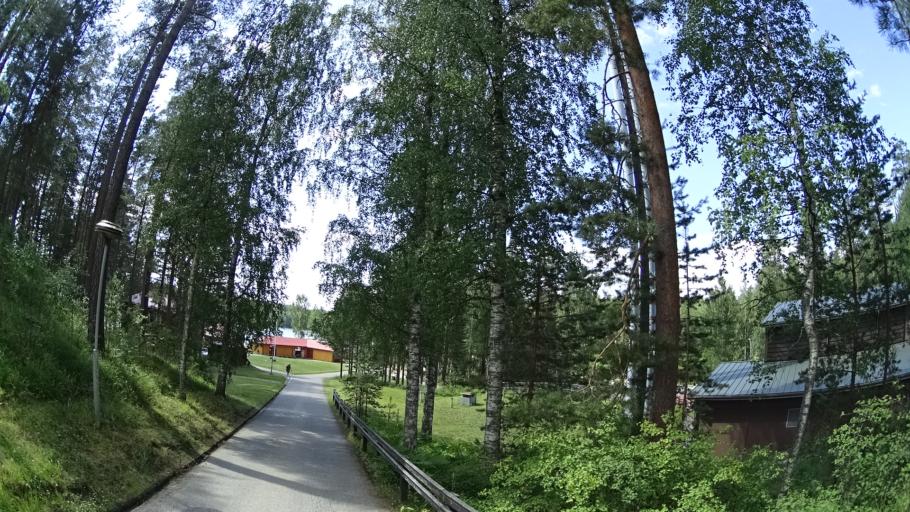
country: FI
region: Southern Savonia
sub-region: Savonlinna
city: Punkaharju
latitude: 61.7855
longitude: 29.3107
